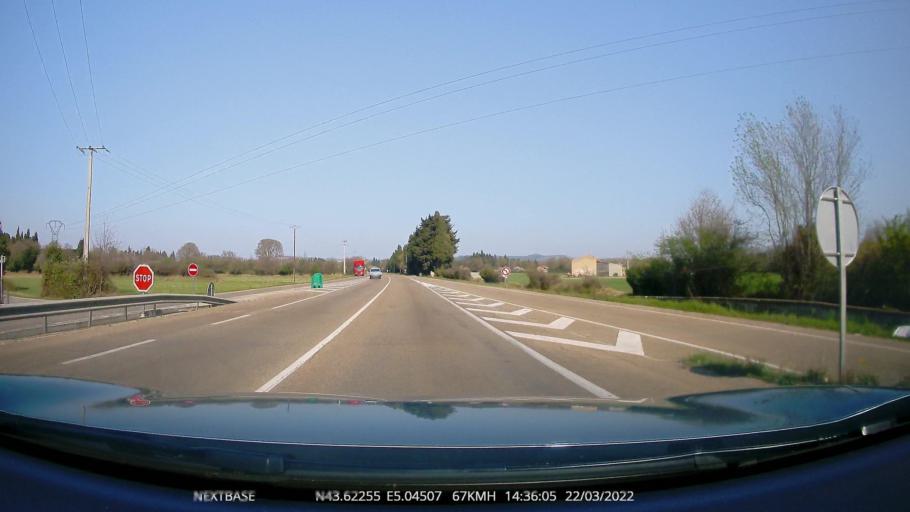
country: FR
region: Provence-Alpes-Cote d'Azur
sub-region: Departement des Bouches-du-Rhone
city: Grans
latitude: 43.6226
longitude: 5.0452
